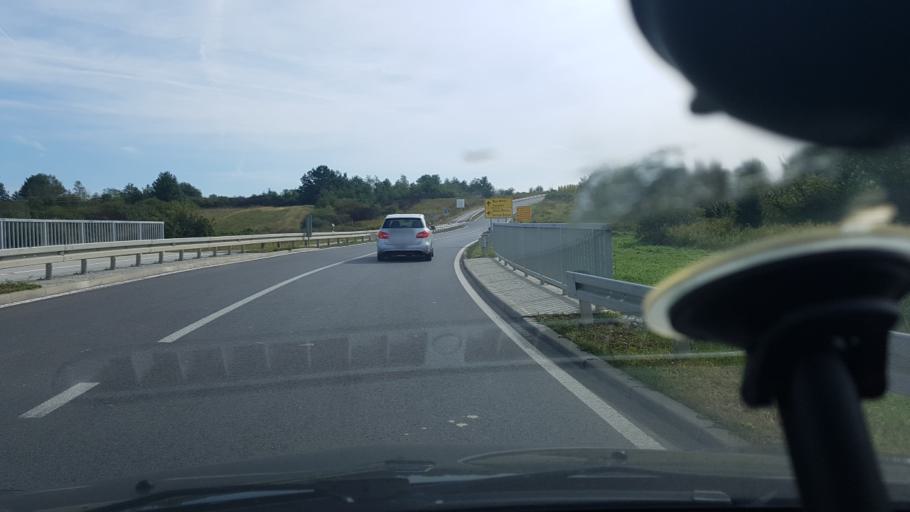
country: HR
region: Krapinsko-Zagorska
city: Marija Bistrica
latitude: 46.0585
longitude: 16.1593
